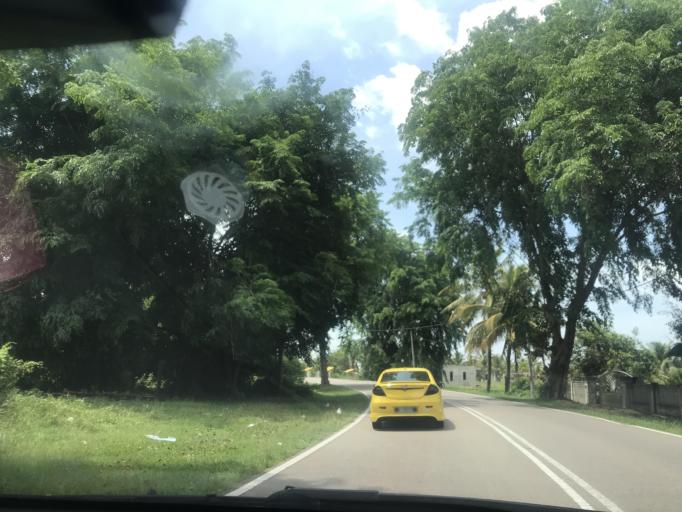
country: MY
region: Kelantan
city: Tumpat
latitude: 6.2018
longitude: 102.1502
